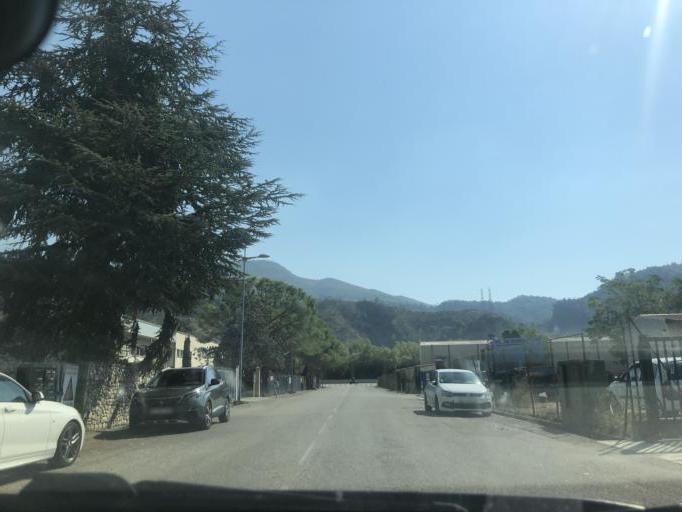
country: FR
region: Provence-Alpes-Cote d'Azur
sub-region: Departement des Alpes-Maritimes
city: Colomars
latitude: 43.7773
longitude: 7.2112
